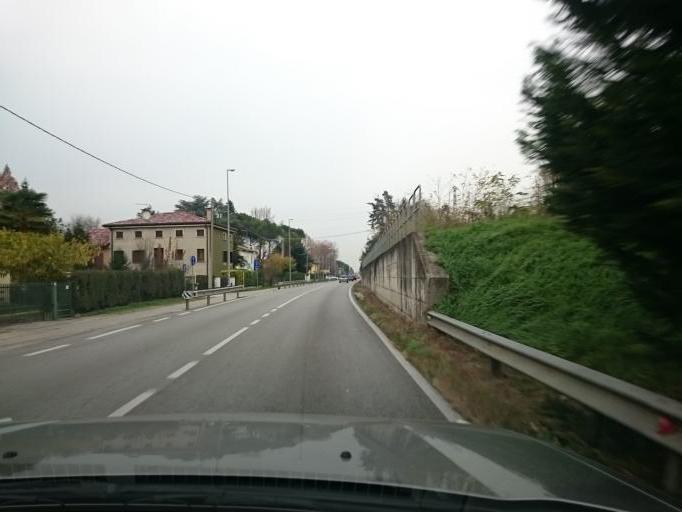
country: IT
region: Veneto
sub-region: Provincia di Padova
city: Sarmeola
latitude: 45.4289
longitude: 11.8266
